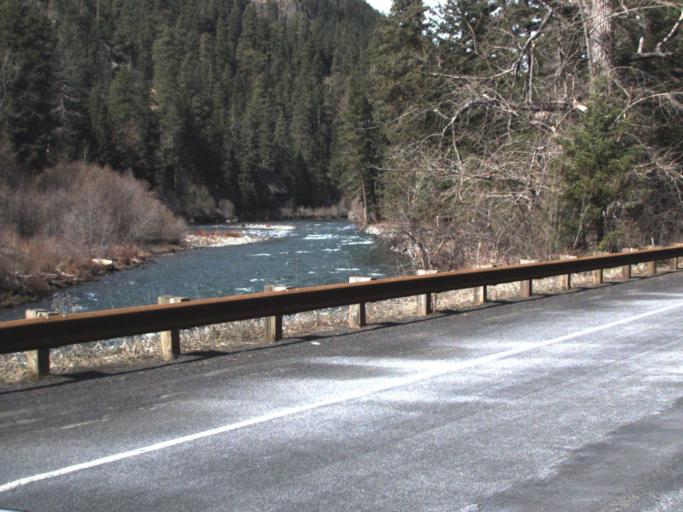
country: US
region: Washington
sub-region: Kittitas County
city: Cle Elum
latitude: 46.9370
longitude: -121.0596
